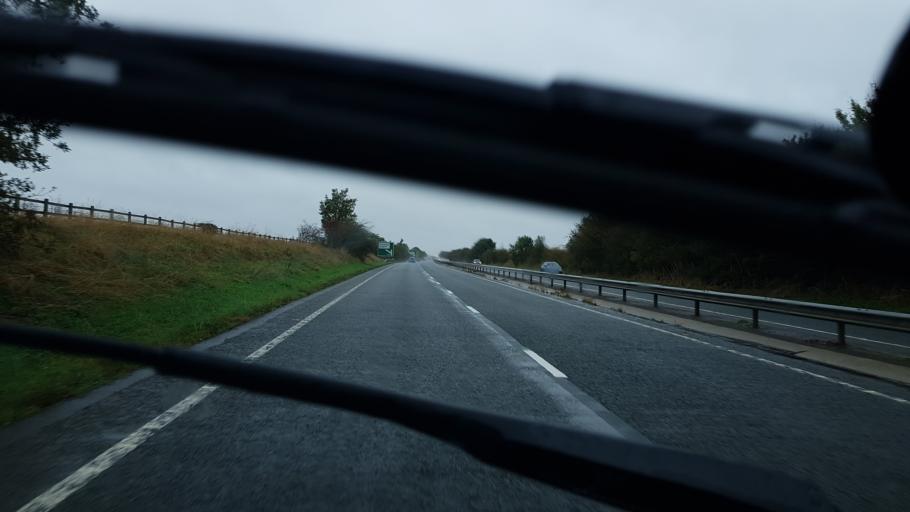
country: GB
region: England
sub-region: Oxfordshire
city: Witney
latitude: 51.7799
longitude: -1.5348
